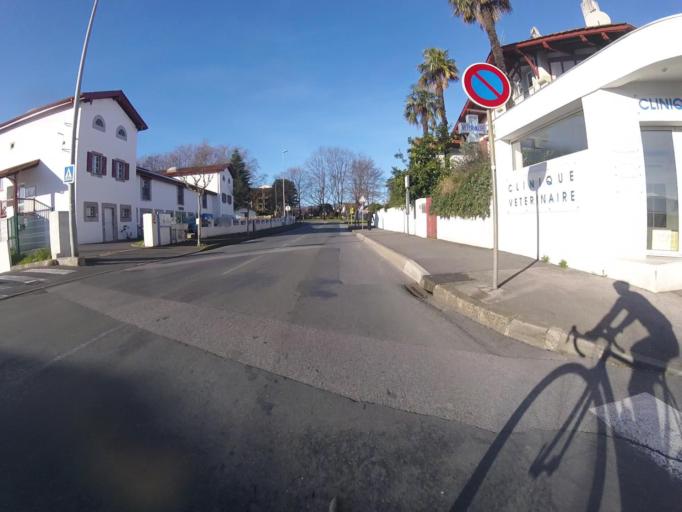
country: FR
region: Aquitaine
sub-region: Departement des Pyrenees-Atlantiques
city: Hendaye
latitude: 43.3536
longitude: -1.7743
